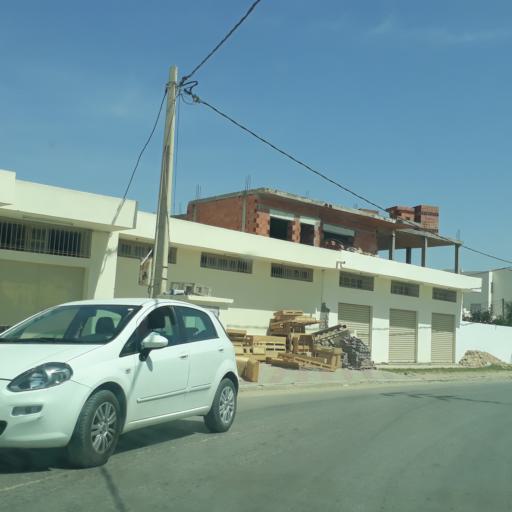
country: TN
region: Safaqis
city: Al Qarmadah
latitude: 34.8149
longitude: 10.7720
